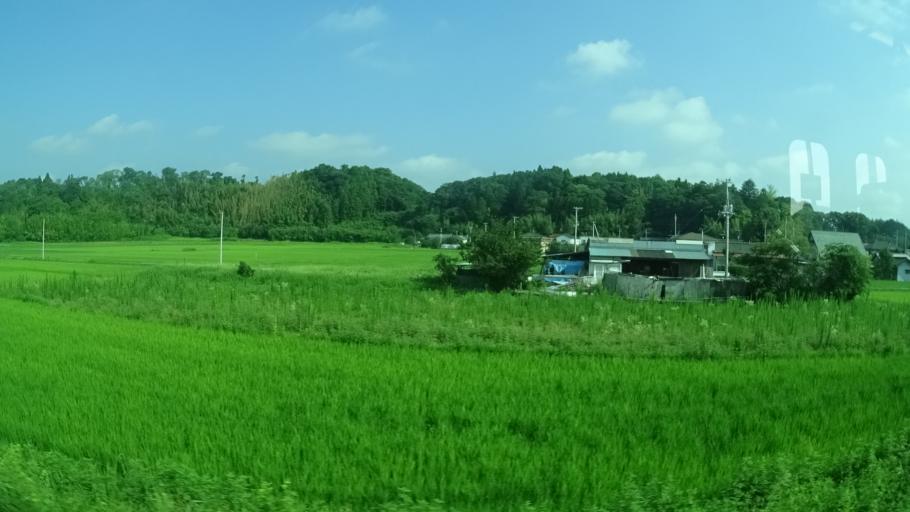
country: JP
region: Fukushima
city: Iwaki
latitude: 37.0675
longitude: 140.9374
